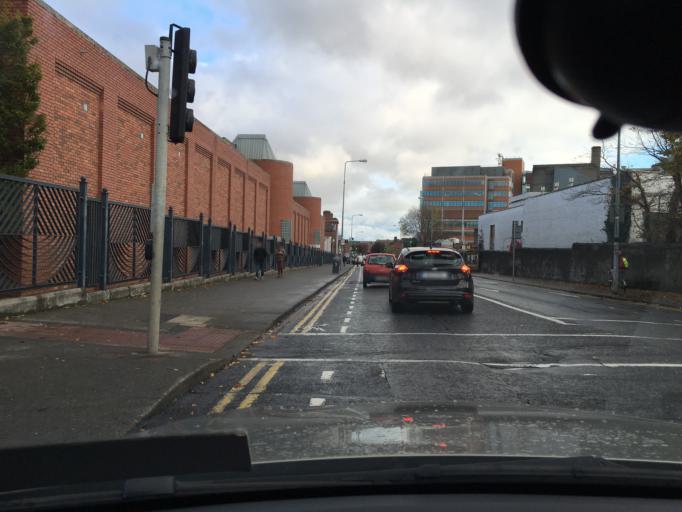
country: IE
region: Leinster
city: Drumcondra
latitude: 53.3606
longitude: -6.2694
